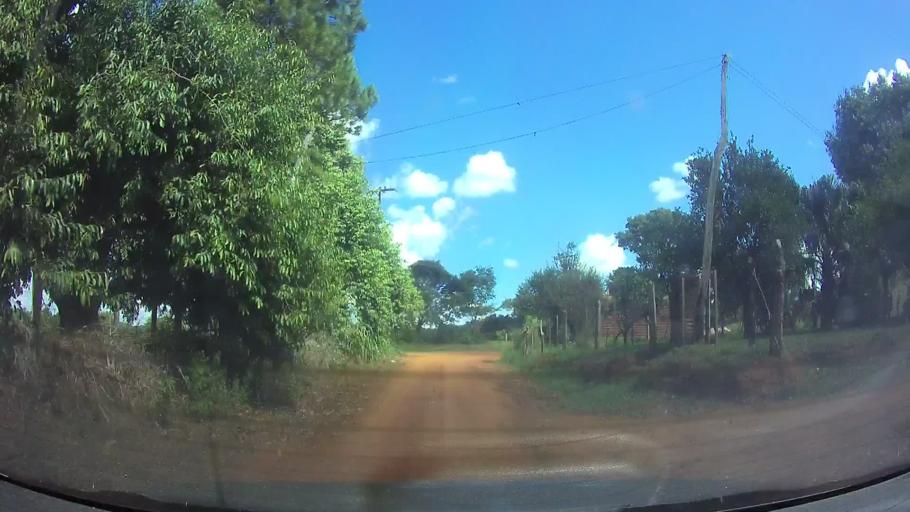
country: PY
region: Paraguari
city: La Colmena
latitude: -25.9416
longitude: -56.7790
